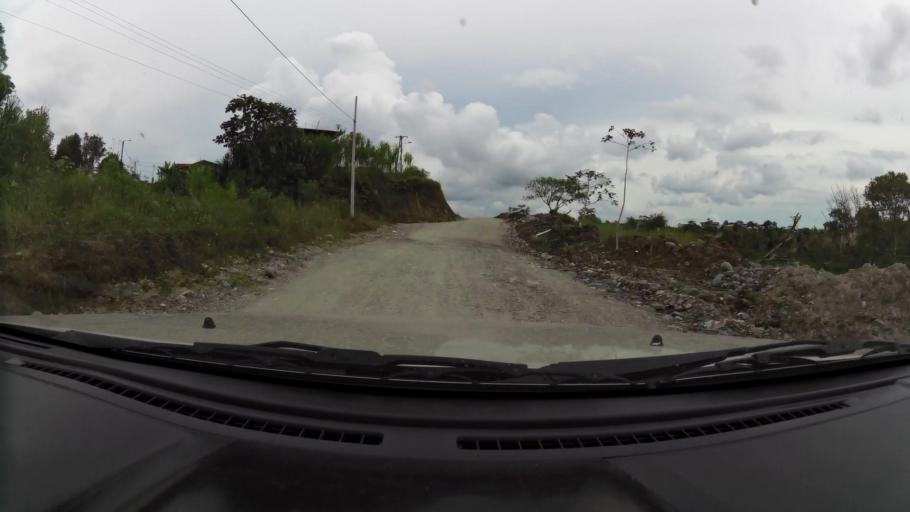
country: EC
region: Pastaza
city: Puyo
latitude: -1.4949
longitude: -78.0047
